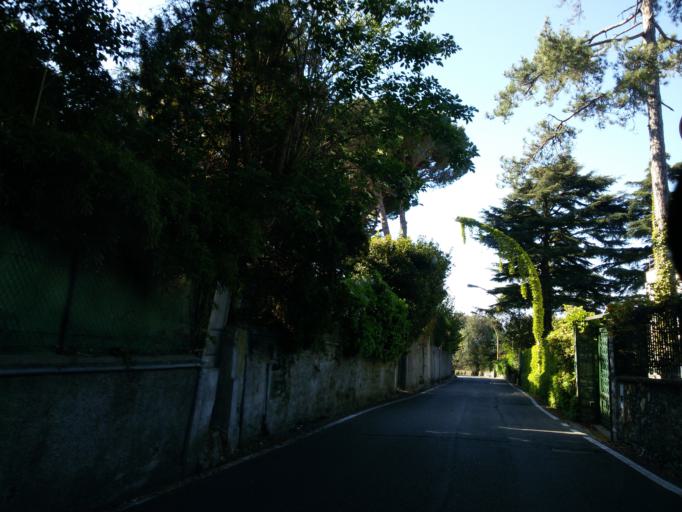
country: IT
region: Liguria
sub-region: Provincia di Genova
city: Bogliasco
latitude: 44.3888
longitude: 9.0038
